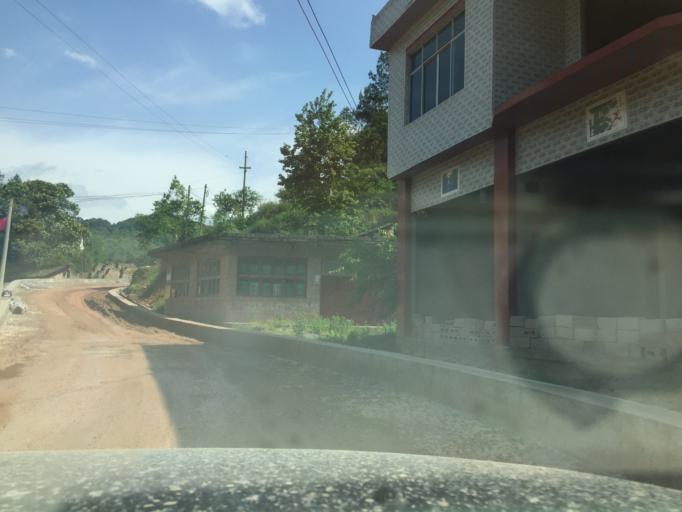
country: CN
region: Guizhou Sheng
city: Fuxing
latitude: 28.0671
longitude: 107.9120
